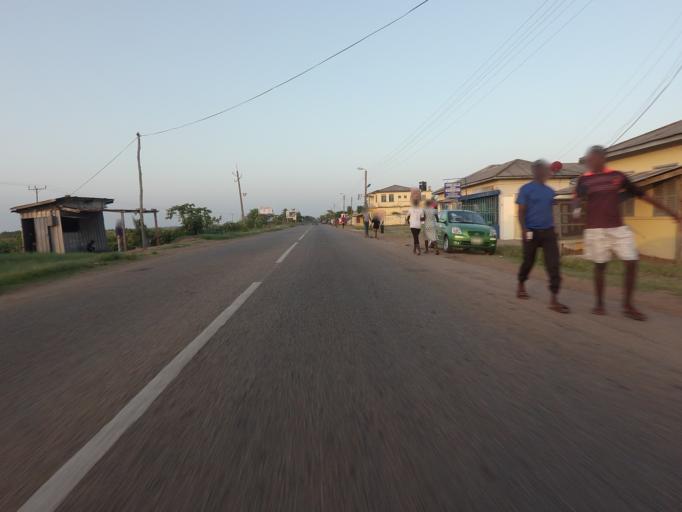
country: GH
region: Volta
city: Anloga
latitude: 5.7975
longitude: 0.9077
